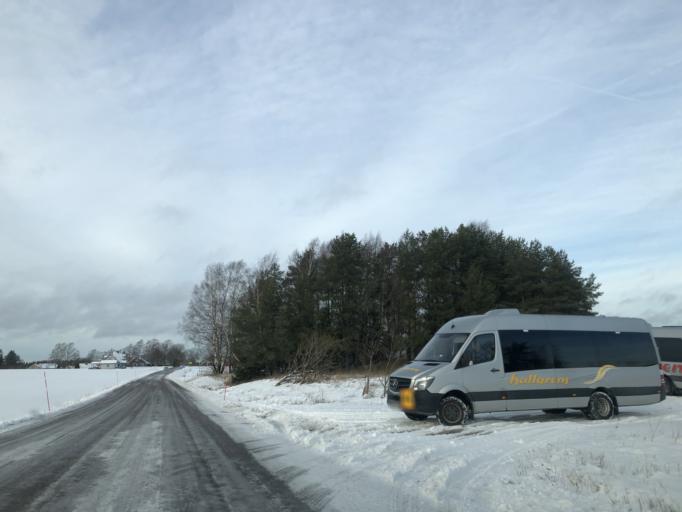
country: SE
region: Vaestra Goetaland
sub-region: Ulricehamns Kommun
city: Ulricehamn
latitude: 57.8153
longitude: 13.5341
